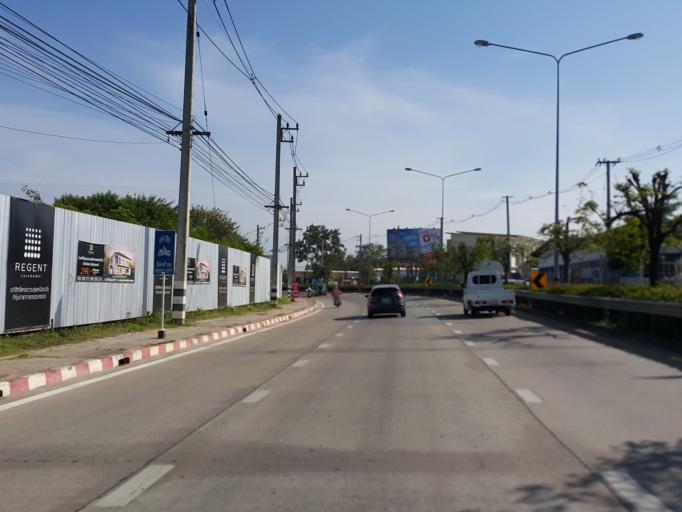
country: TH
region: Chiang Mai
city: Chiang Mai
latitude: 18.8005
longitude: 99.0323
